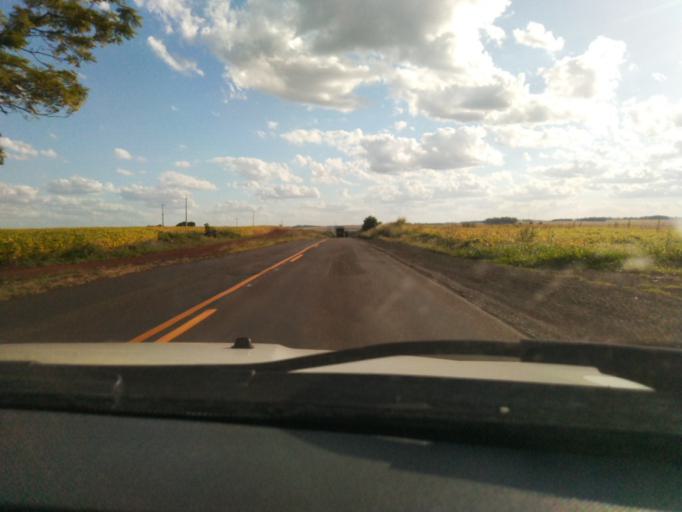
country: AR
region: Corrientes
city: Garruchos
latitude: -28.5521
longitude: -55.5690
